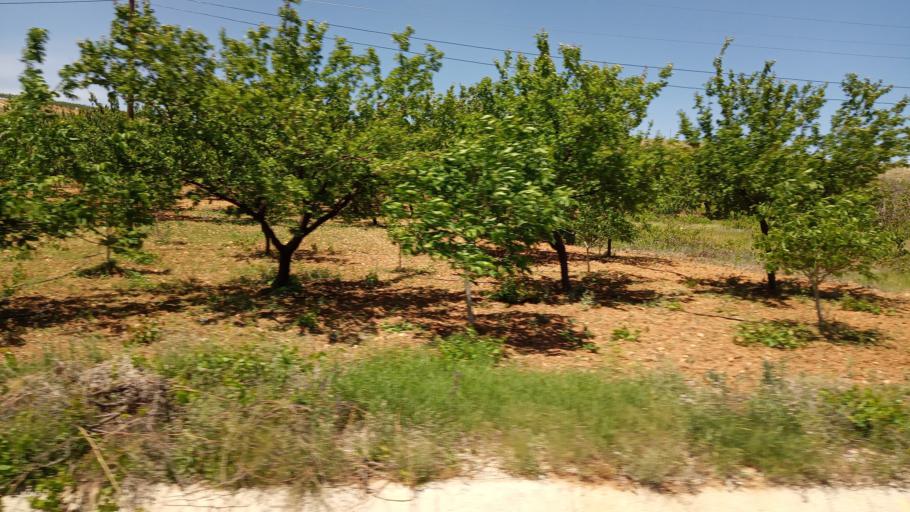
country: TR
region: Malatya
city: Darende
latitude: 38.6006
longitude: 37.4634
